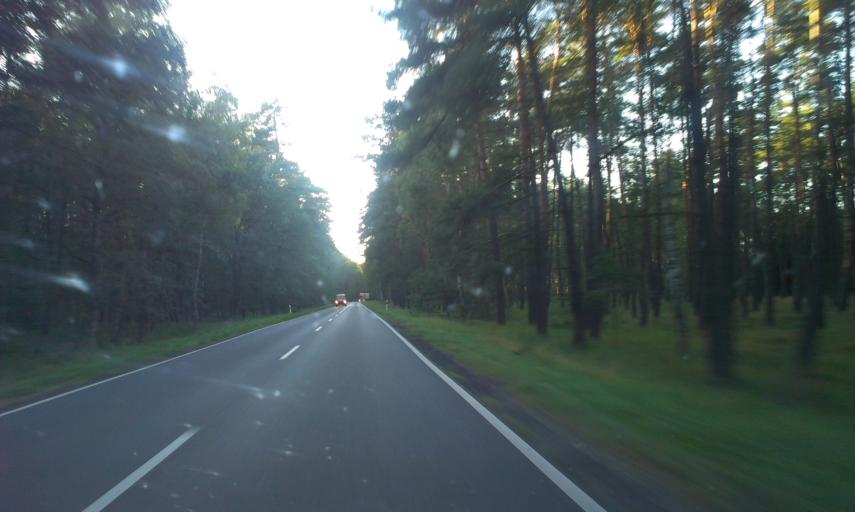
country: PL
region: Pomeranian Voivodeship
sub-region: Powiat czluchowski
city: Czarne
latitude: 53.7063
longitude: 16.8647
